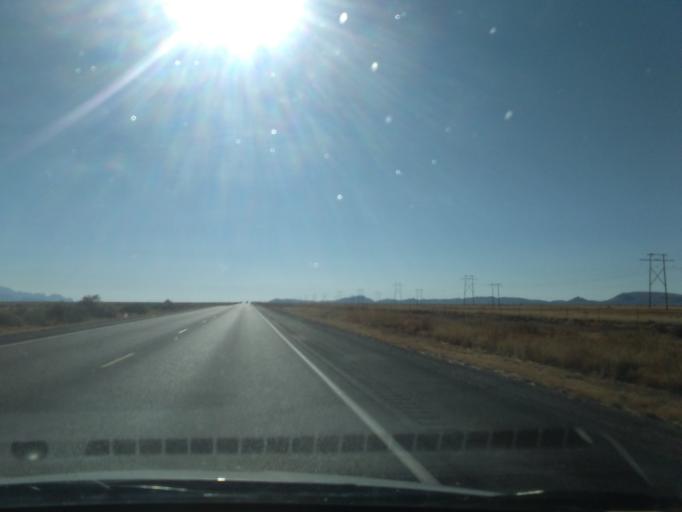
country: US
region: New Mexico
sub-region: Luna County
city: Deming
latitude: 32.4764
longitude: -107.5313
